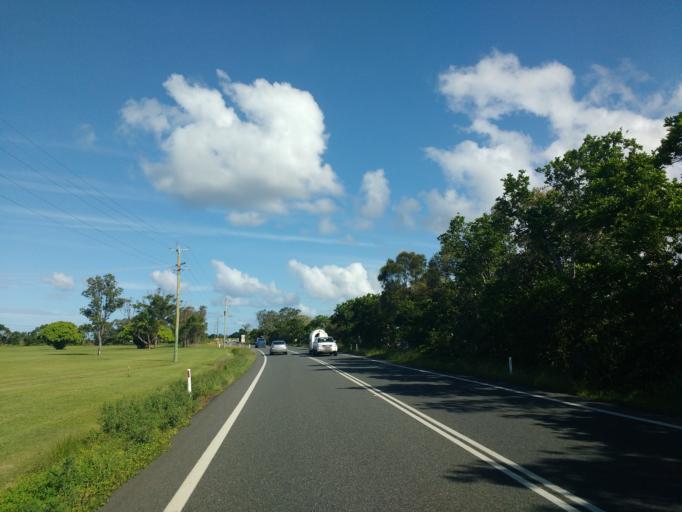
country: AU
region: New South Wales
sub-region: Richmond Valley
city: Evans Head
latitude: -28.9850
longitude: 153.4620
